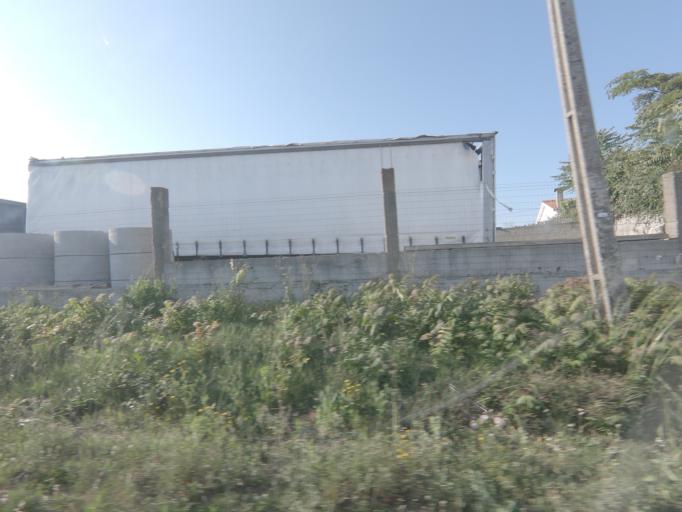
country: PT
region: Vila Real
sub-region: Sabrosa
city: Vilela
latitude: 41.2676
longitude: -7.6300
